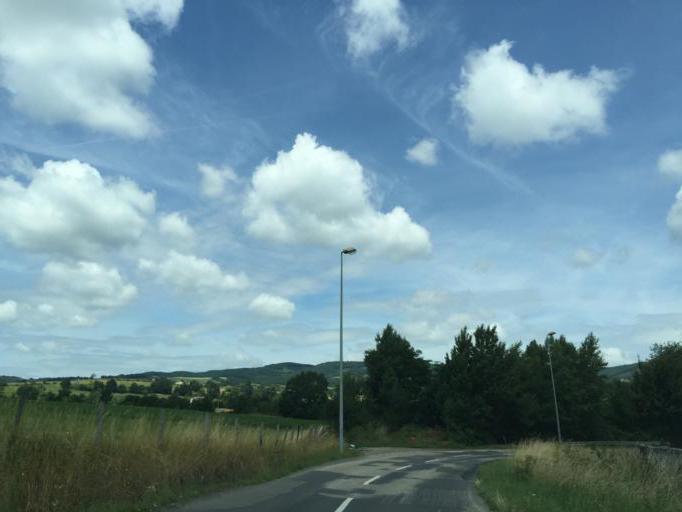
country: FR
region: Rhone-Alpes
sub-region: Departement de la Loire
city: La Grand-Croix
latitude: 45.4937
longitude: 4.5325
